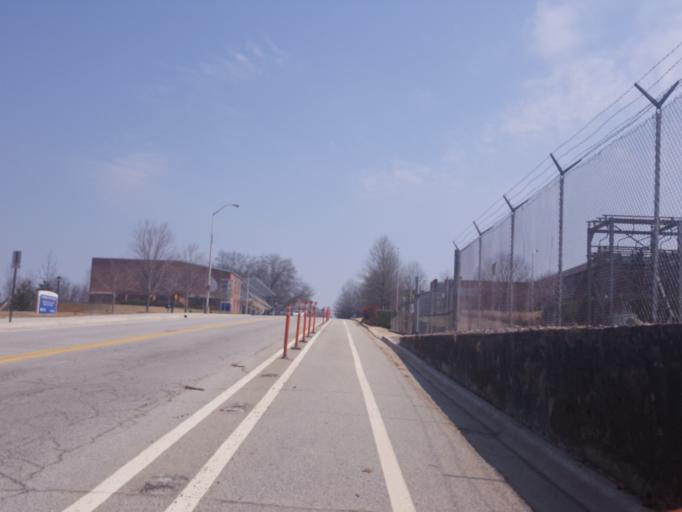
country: US
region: Georgia
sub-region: Carroll County
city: Carrollton
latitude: 33.5754
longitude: -85.1005
